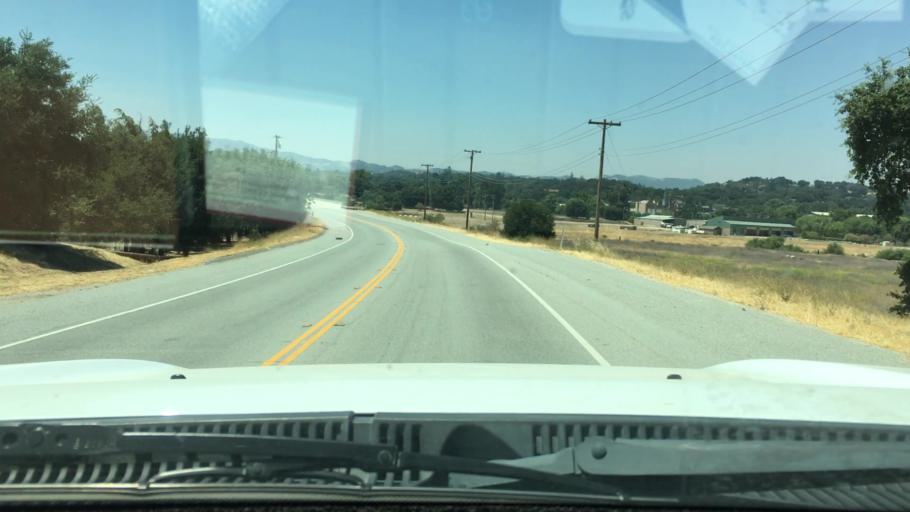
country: US
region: California
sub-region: San Luis Obispo County
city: Atascadero
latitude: 35.5031
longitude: -120.6560
